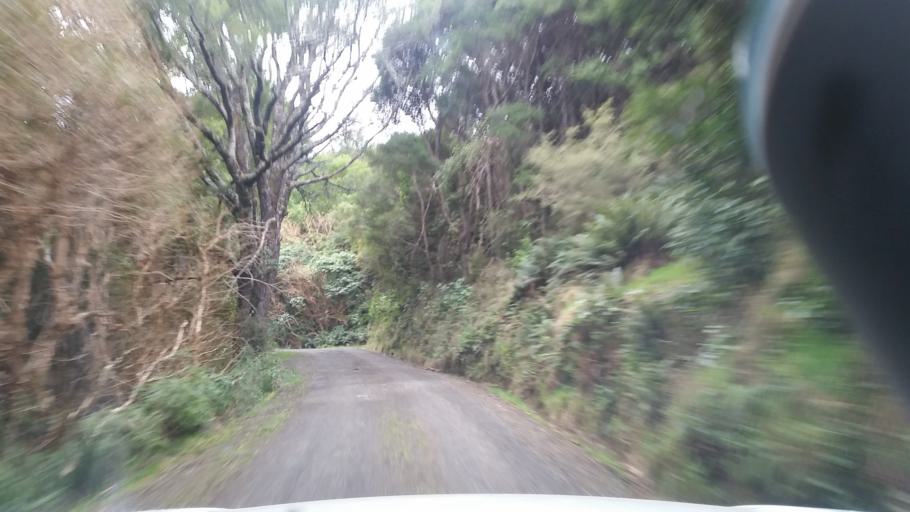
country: NZ
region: Canterbury
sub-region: Christchurch City
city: Christchurch
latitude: -43.8358
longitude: 173.0046
